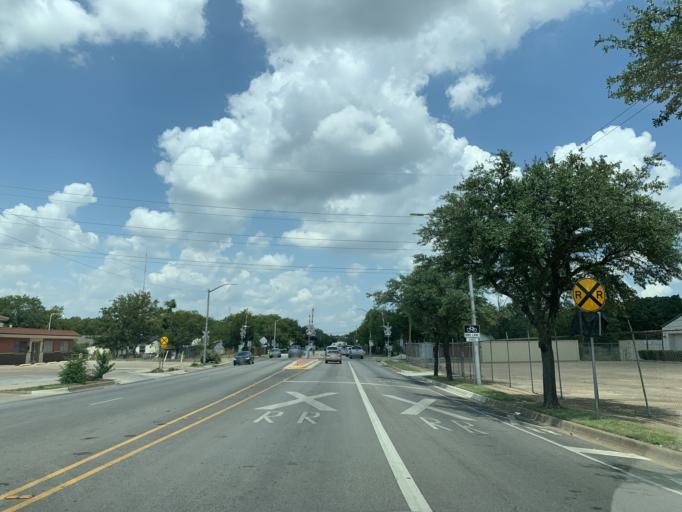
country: US
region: Texas
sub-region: Tarrant County
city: Fort Worth
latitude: 32.7335
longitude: -97.2619
